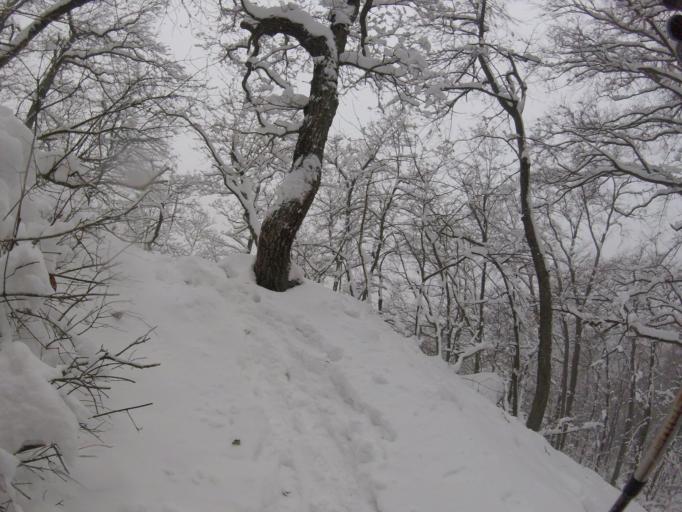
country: HU
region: Komarom-Esztergom
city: Pilismarot
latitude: 47.7386
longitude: 18.8735
